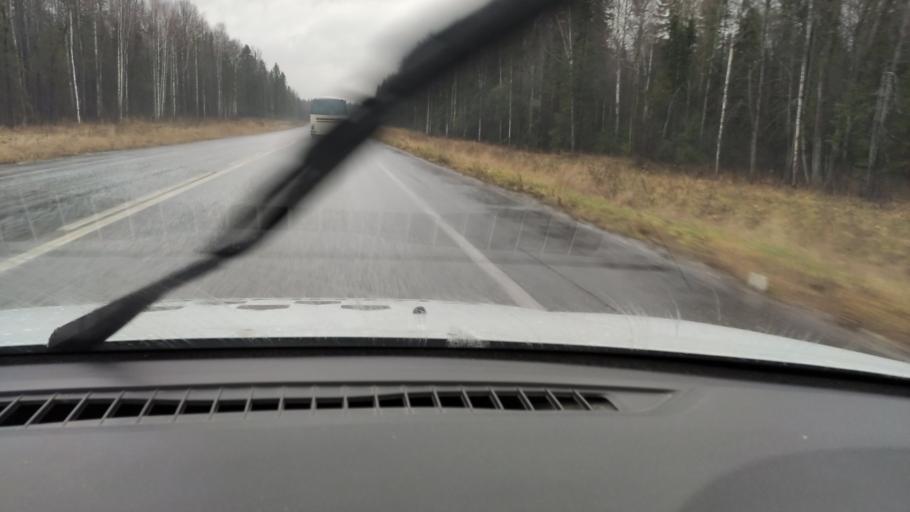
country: RU
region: Perm
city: Novyye Lyady
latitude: 58.0384
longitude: 56.5374
